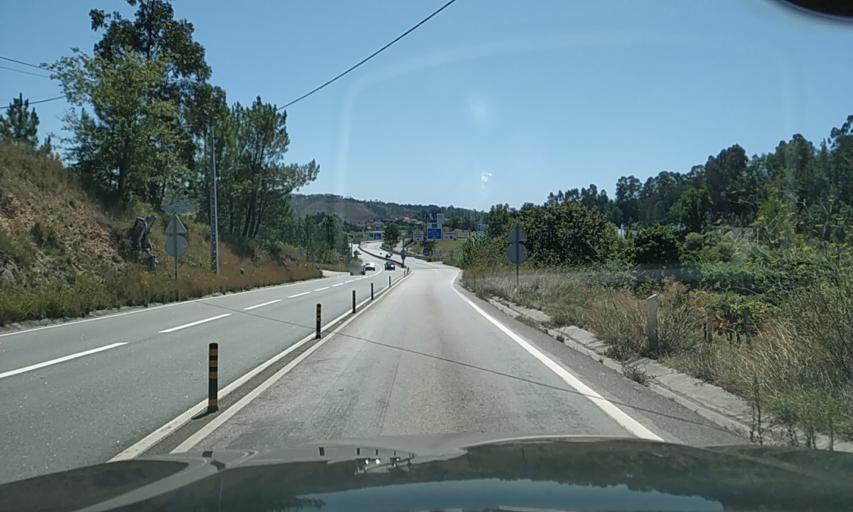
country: PT
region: Aveiro
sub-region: Mealhada
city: Pampilhosa do Botao
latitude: 40.2787
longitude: -8.4461
